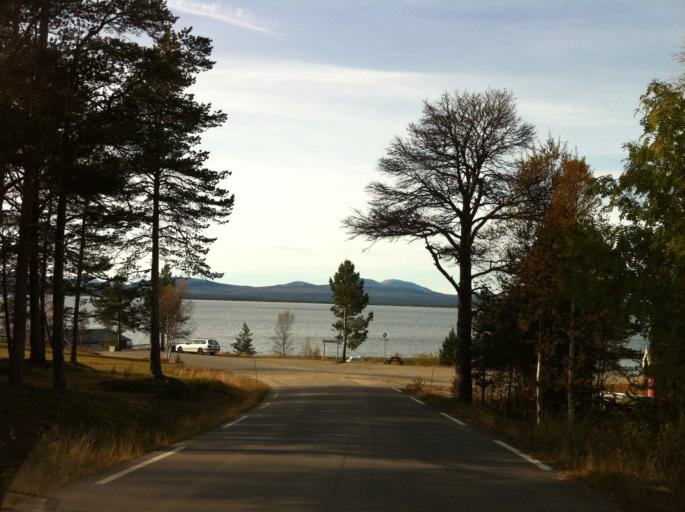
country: NO
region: Hedmark
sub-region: Engerdal
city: Engerdal
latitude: 62.1561
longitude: 11.9485
